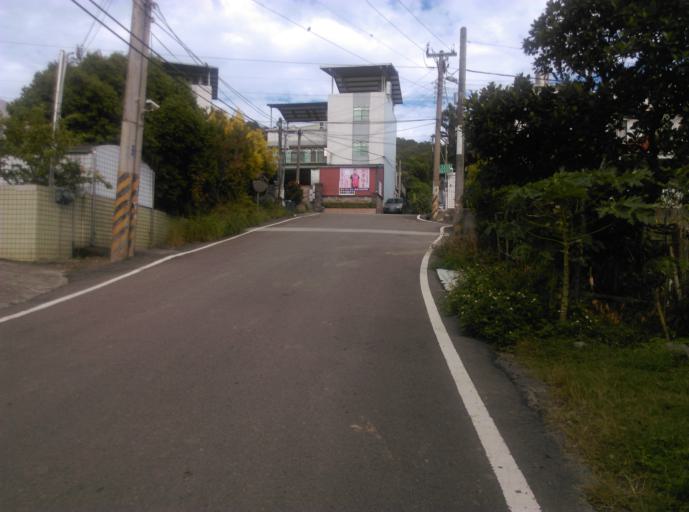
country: TW
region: Taiwan
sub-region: Miaoli
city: Miaoli
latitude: 24.6512
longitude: 120.8845
